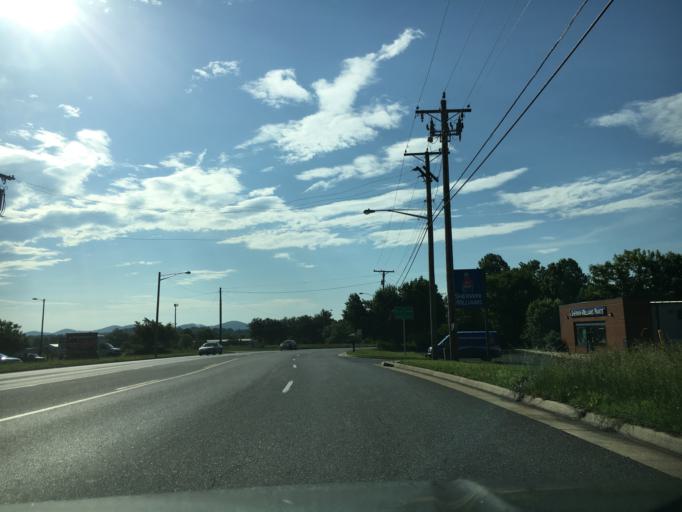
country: US
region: Virginia
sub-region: Bedford County
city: Forest
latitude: 37.3672
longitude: -79.2508
